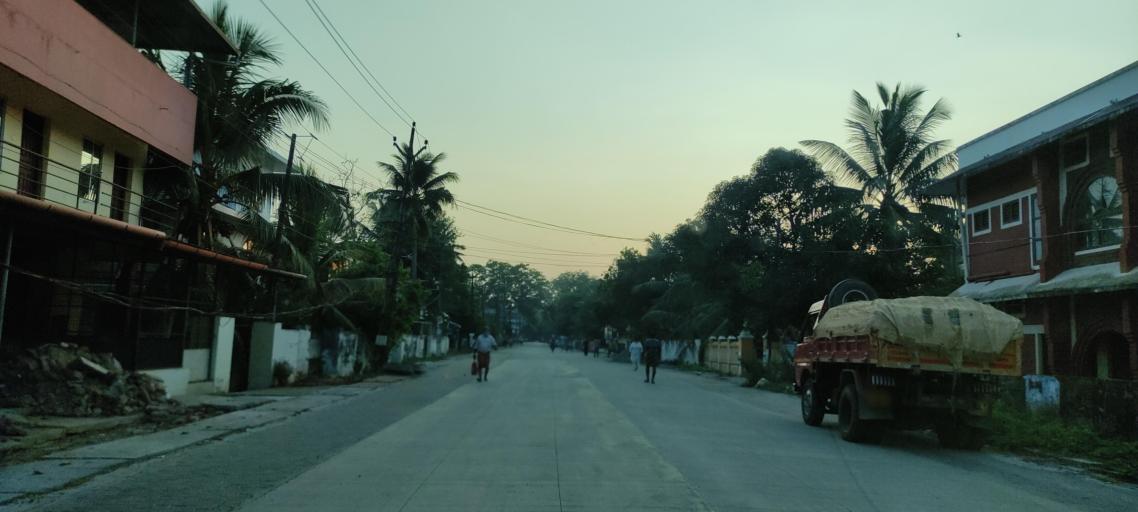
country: IN
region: Kerala
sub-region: Alappuzha
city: Alleppey
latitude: 9.4664
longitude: 76.3396
